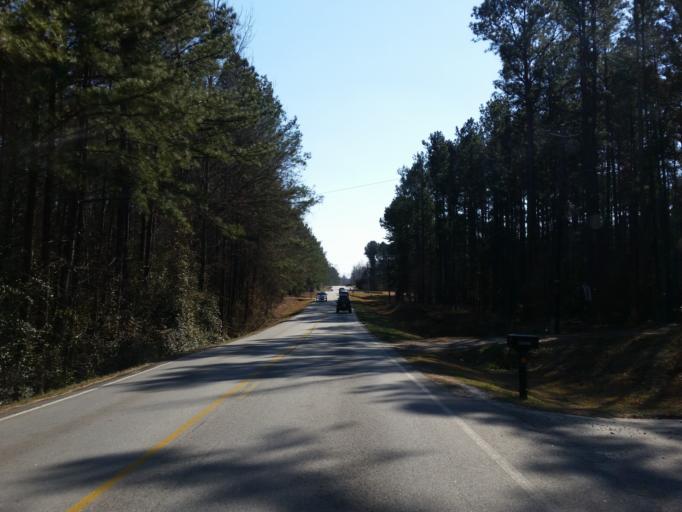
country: US
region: Georgia
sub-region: Henry County
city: Stockbridge
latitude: 33.4834
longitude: -84.2453
